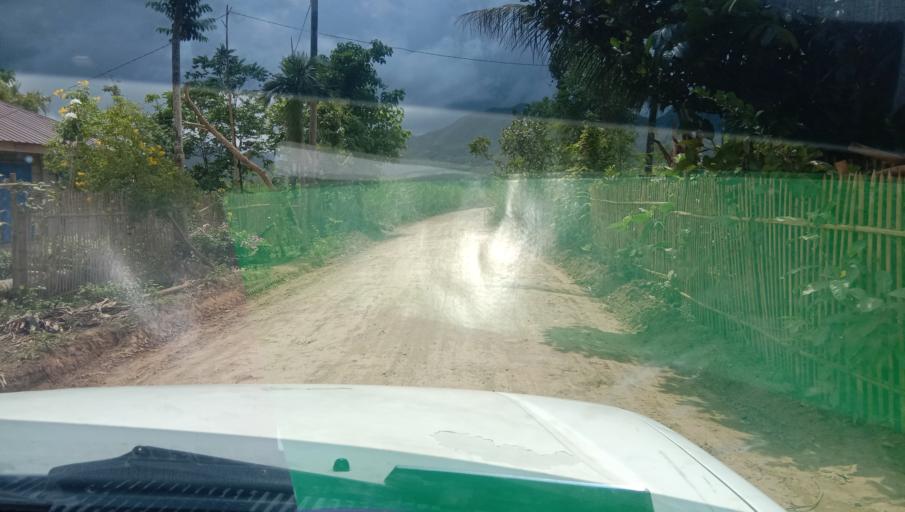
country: PH
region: Western Visayas
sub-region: Province of Iloilo
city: Balasan
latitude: 11.4693
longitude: 123.0564
